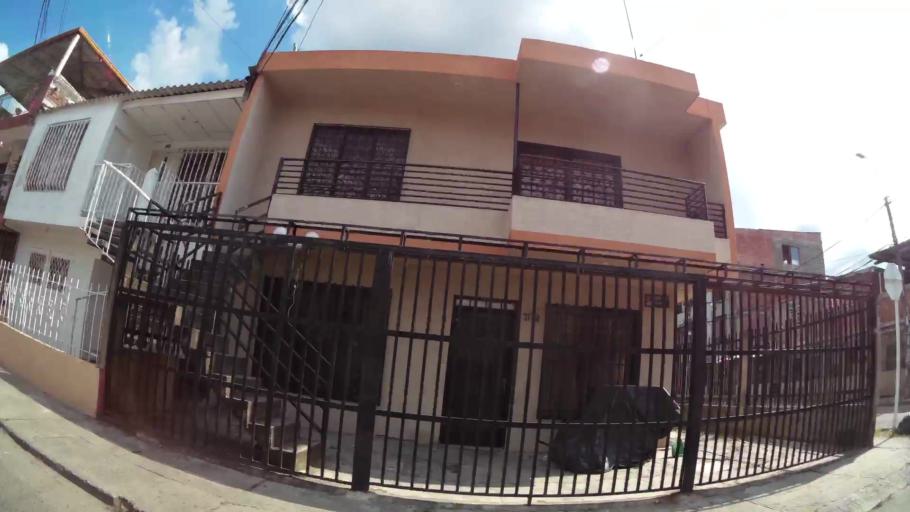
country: CO
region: Valle del Cauca
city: Cali
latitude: 3.4191
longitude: -76.5138
